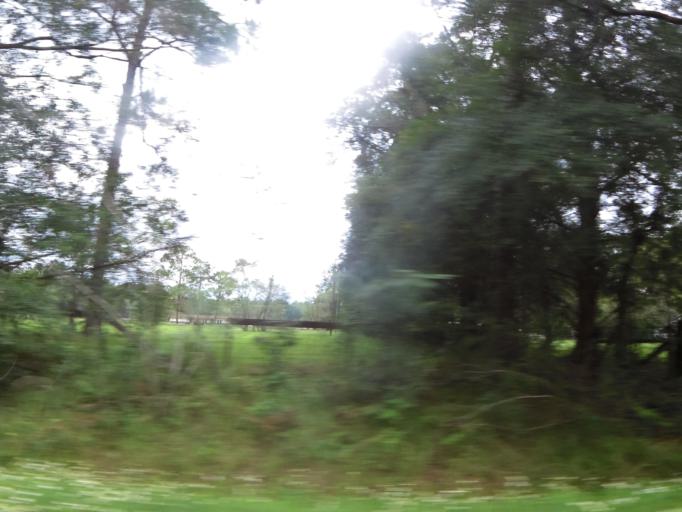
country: US
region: Florida
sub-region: Clay County
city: Middleburg
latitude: 30.1142
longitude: -81.8523
